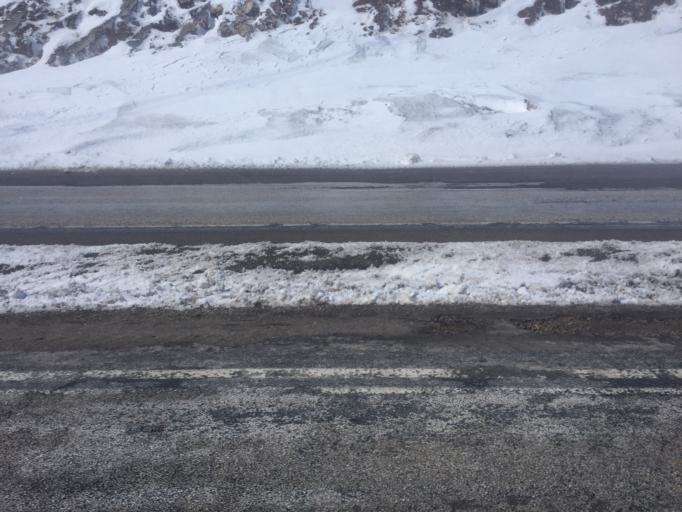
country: TR
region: Kahramanmaras
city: Goksun
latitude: 38.1918
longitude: 36.4569
